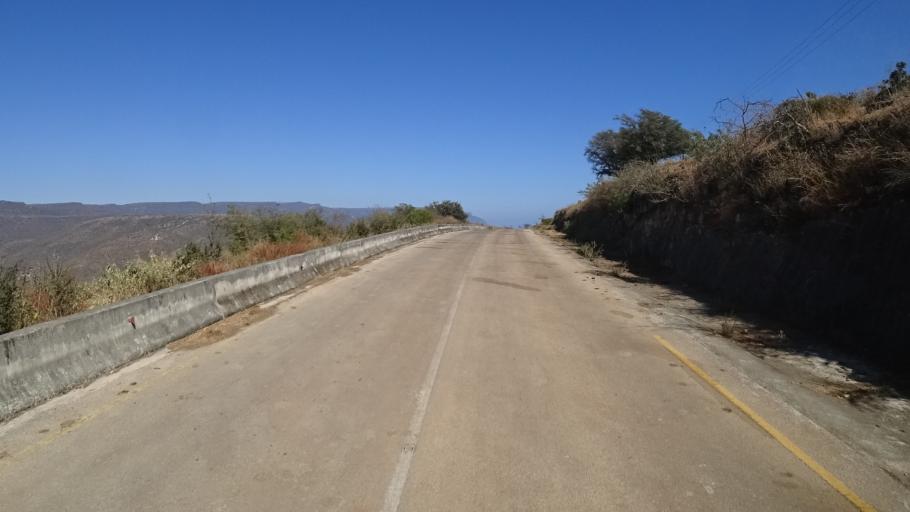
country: YE
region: Al Mahrah
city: Hawf
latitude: 16.7453
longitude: 53.3899
